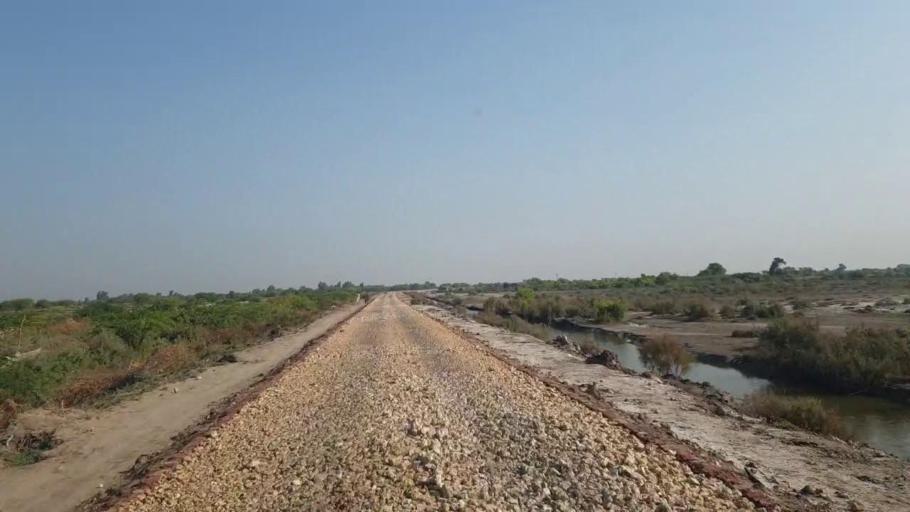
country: PK
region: Sindh
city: Badin
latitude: 24.4894
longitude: 68.7497
